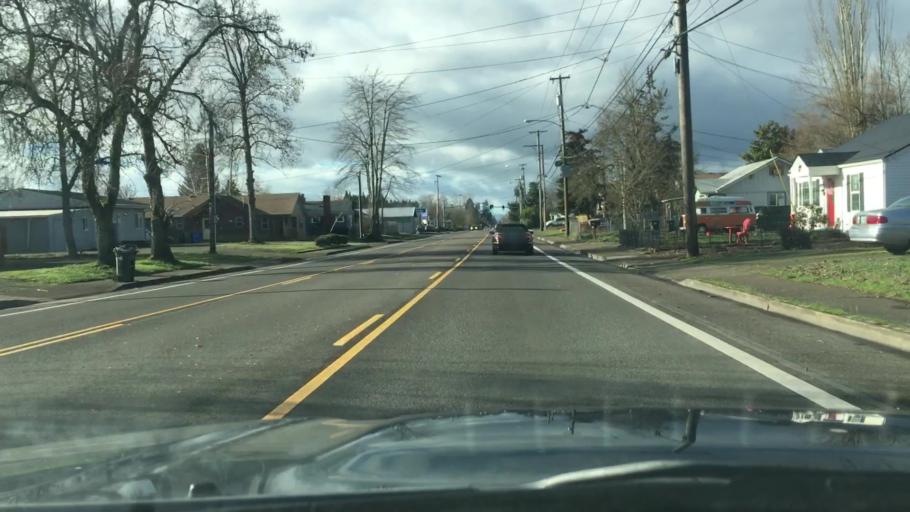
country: US
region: Oregon
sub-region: Lane County
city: Eugene
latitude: 44.0701
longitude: -123.1753
